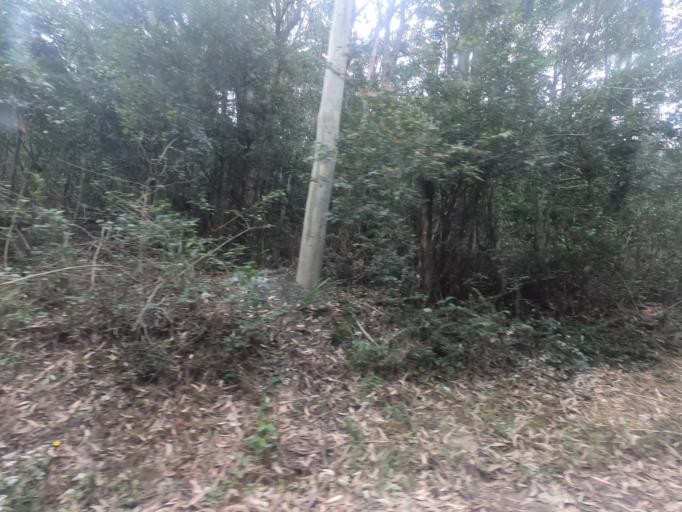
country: AU
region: New South Wales
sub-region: Wollongong
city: Bulli
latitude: -34.2968
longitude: 150.9338
